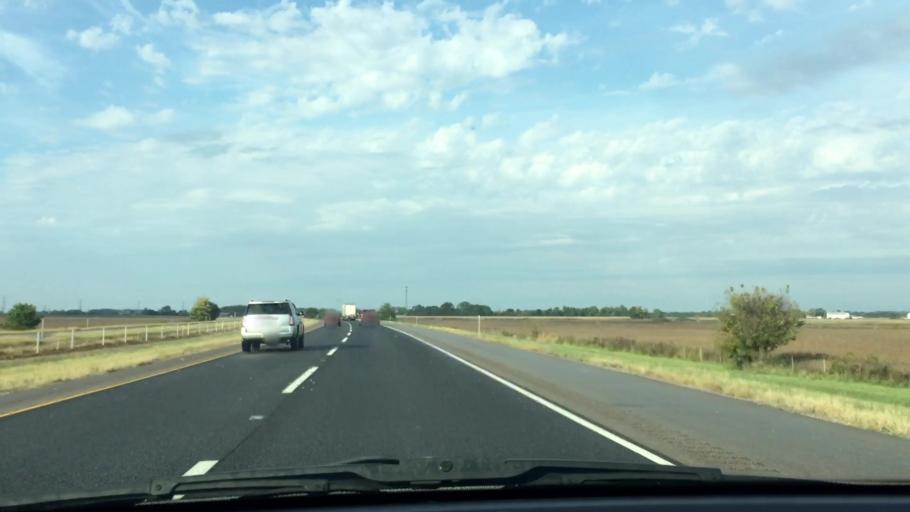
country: US
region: Illinois
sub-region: Lee County
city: Dixon
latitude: 41.7791
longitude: -89.5621
